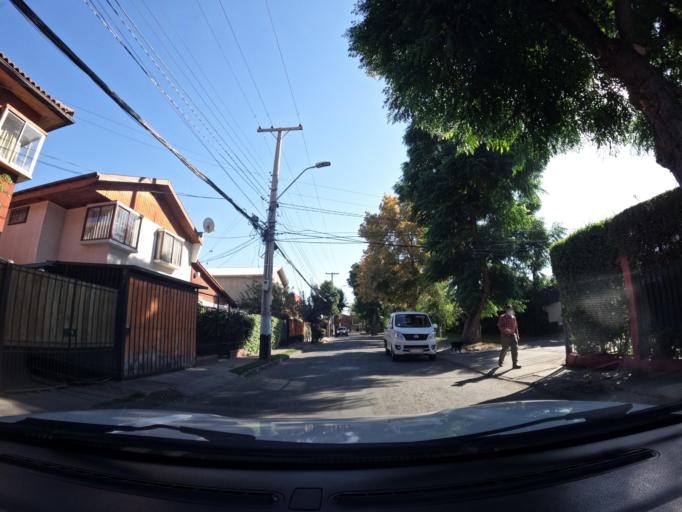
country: CL
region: Santiago Metropolitan
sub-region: Provincia de Santiago
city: Villa Presidente Frei, Nunoa, Santiago, Chile
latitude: -33.5087
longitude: -70.5859
